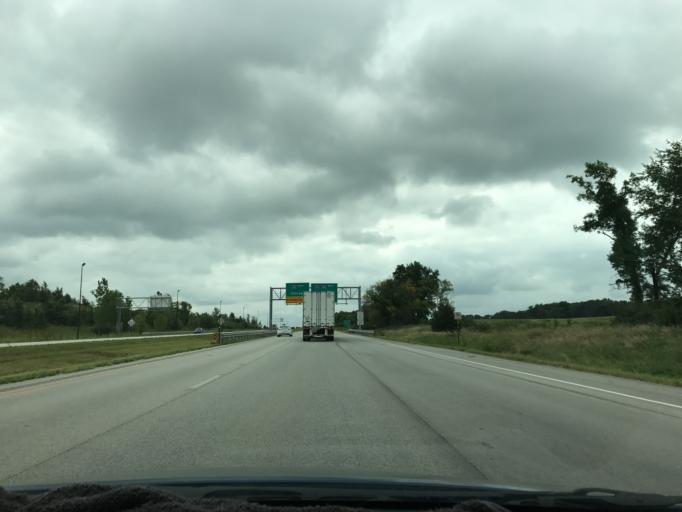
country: US
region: Illinois
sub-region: Henry County
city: Green Rock
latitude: 41.4518
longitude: -90.3354
